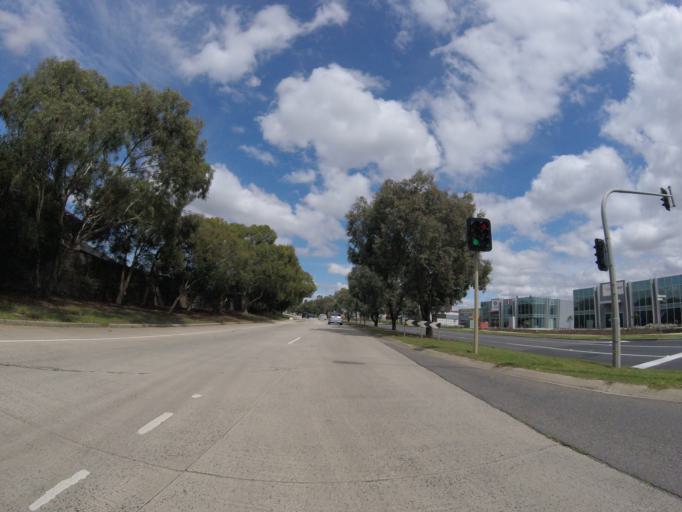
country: AU
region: Victoria
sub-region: Brimbank
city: Keilor Park
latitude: -37.7201
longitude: 144.8516
